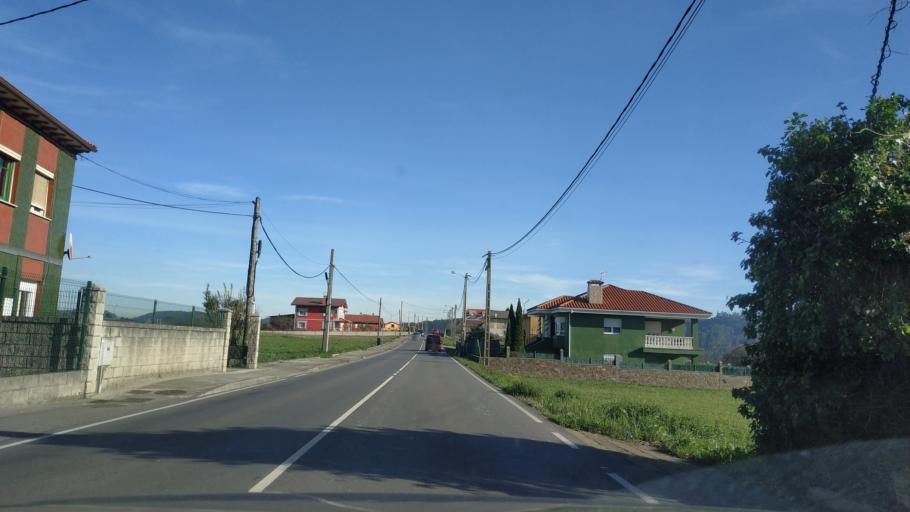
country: ES
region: Asturias
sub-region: Province of Asturias
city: Corvera de Asturias
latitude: 43.5384
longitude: -5.8881
